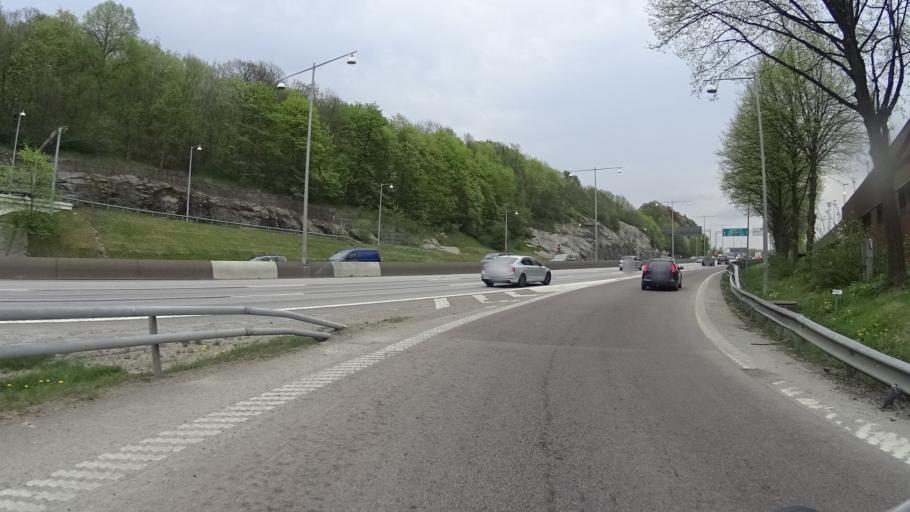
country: SE
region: Vaestra Goetaland
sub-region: Goteborg
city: Goeteborg
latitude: 57.7062
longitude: 11.9953
